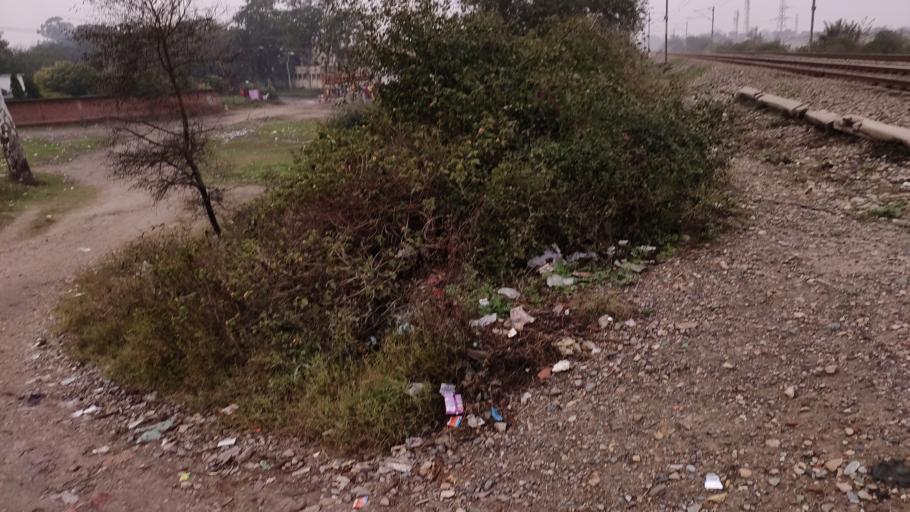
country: IN
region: Punjab
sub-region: Amritsar
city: Amritsar
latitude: 31.6227
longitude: 74.9285
